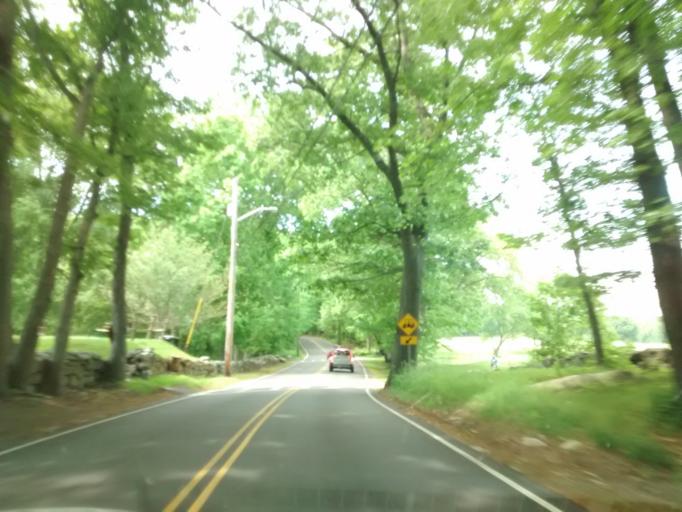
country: US
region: Massachusetts
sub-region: Worcester County
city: Whitinsville
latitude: 42.1002
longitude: -71.6591
